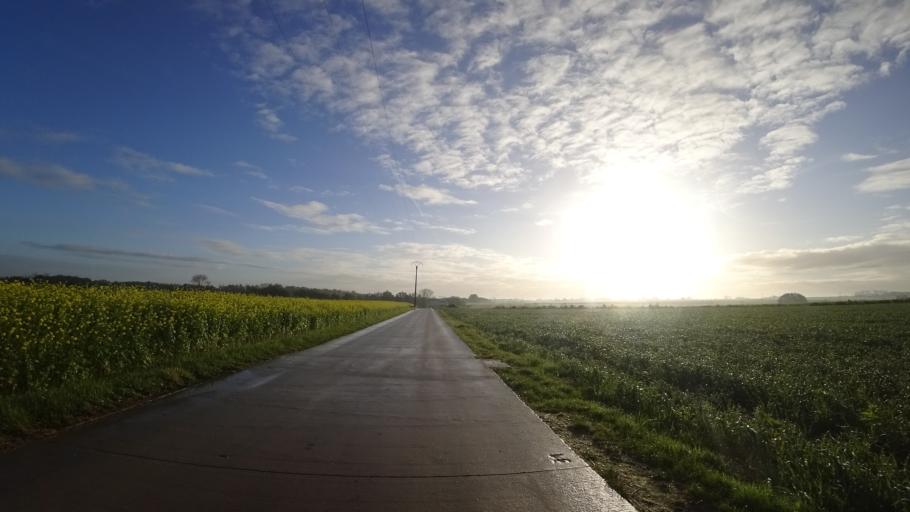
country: BE
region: Wallonia
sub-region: Province de Namur
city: Gembloux
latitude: 50.5509
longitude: 4.7527
